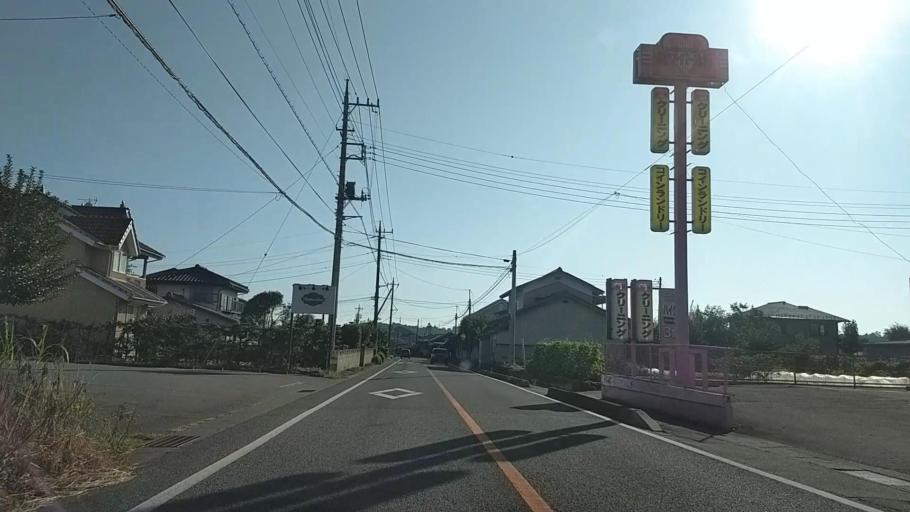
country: JP
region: Gunma
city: Annaka
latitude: 36.3162
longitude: 138.8836
